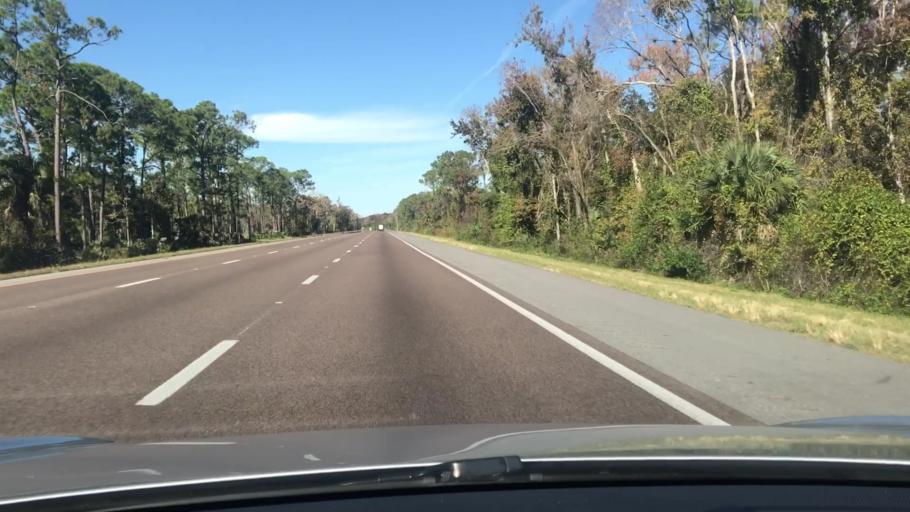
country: US
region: Florida
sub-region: Volusia County
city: Edgewater
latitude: 28.9162
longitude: -80.9358
